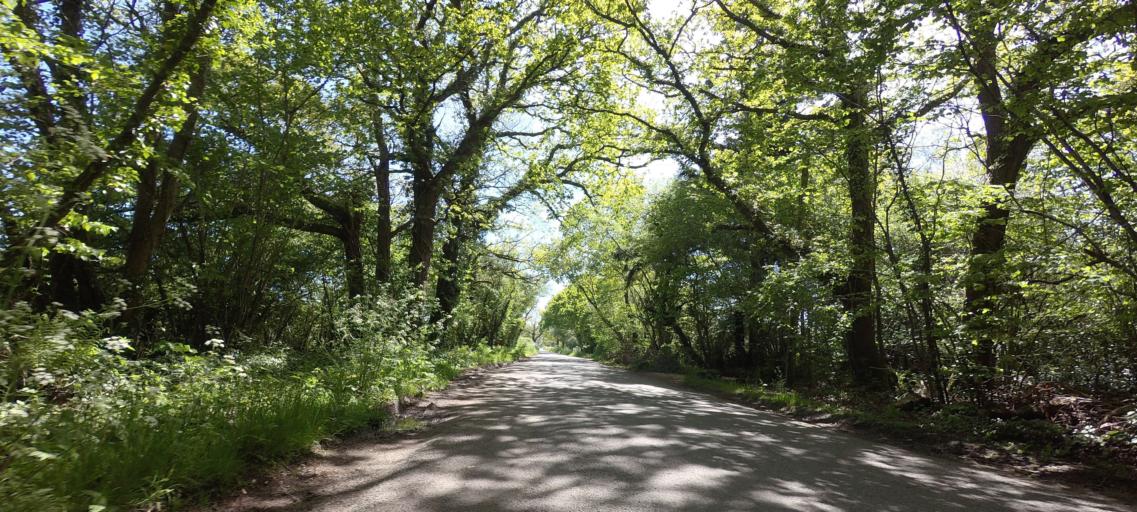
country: GB
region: England
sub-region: Dorset
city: Bovington Camp
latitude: 50.6756
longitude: -2.3287
